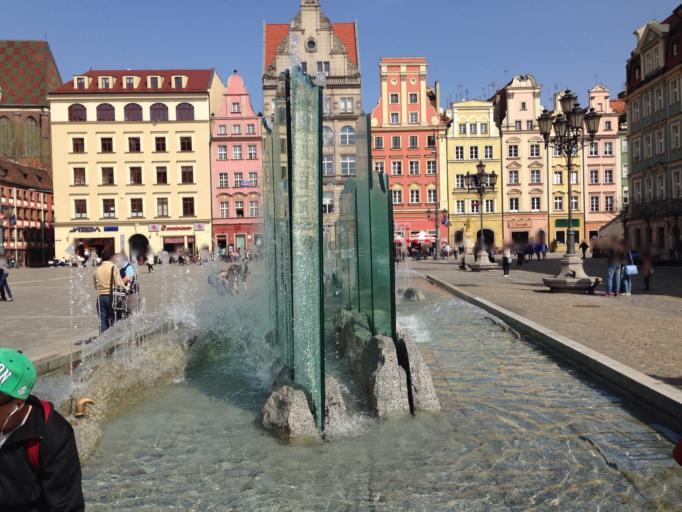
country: PL
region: Lower Silesian Voivodeship
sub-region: Powiat wroclawski
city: Wroclaw
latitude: 51.1103
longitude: 17.0310
